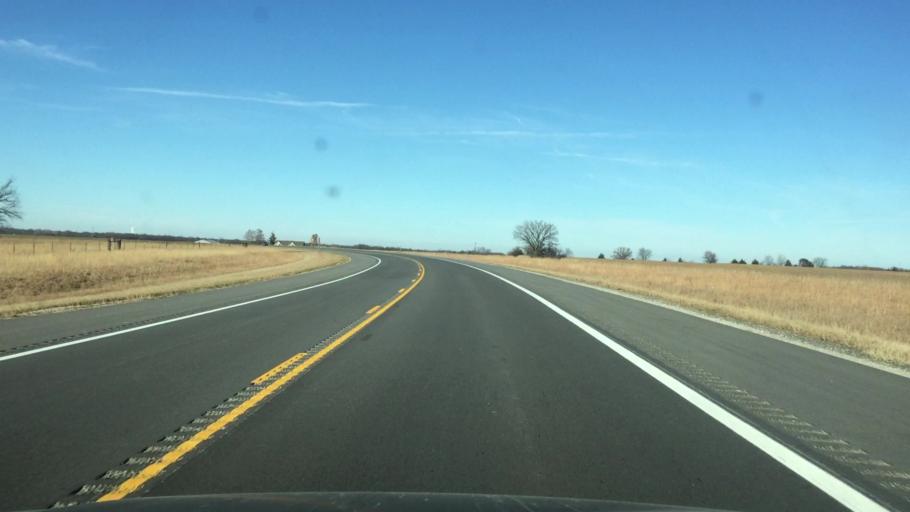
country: US
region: Kansas
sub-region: Franklin County
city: Ottawa
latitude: 38.4571
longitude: -95.2488
